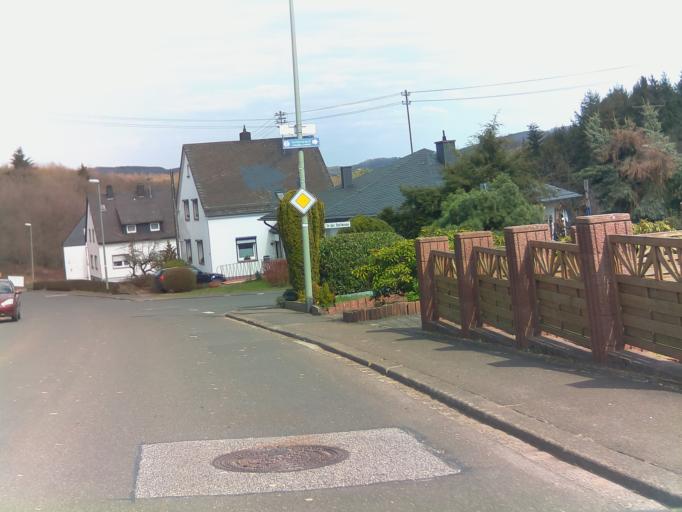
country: DE
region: Rheinland-Pfalz
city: Hettenrodt
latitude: 49.7416
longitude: 7.2547
